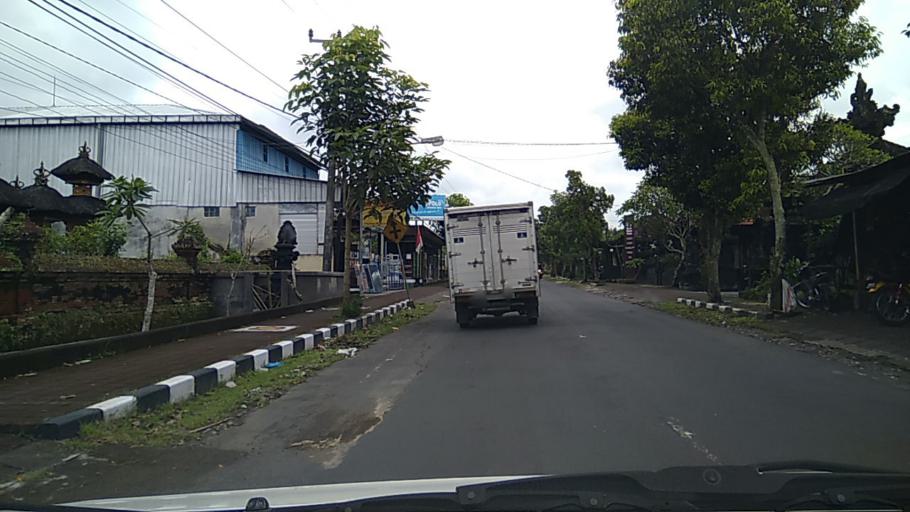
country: ID
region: Bali
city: Brahmana
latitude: -8.4911
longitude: 115.2099
